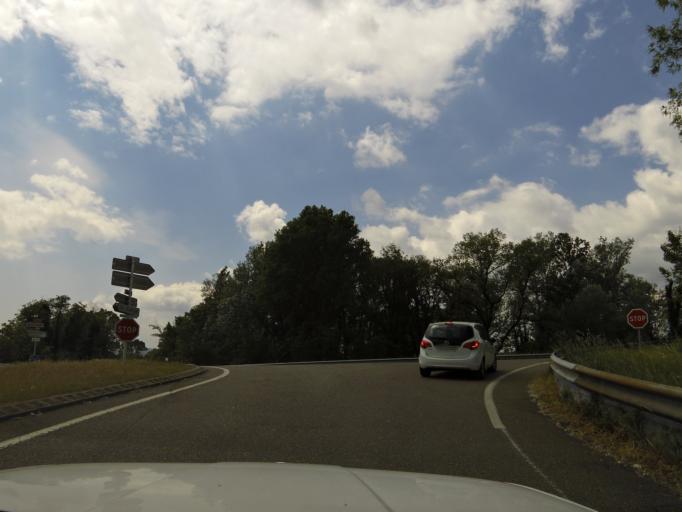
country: FR
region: Rhone-Alpes
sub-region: Departement de la Drome
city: Ancone
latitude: 44.5760
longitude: 4.7207
